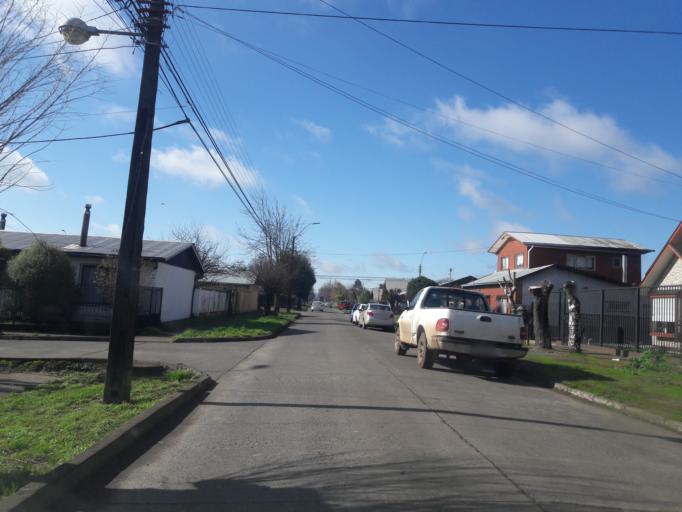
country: CL
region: Araucania
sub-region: Provincia de Malleco
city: Victoria
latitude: -38.2325
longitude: -72.3388
